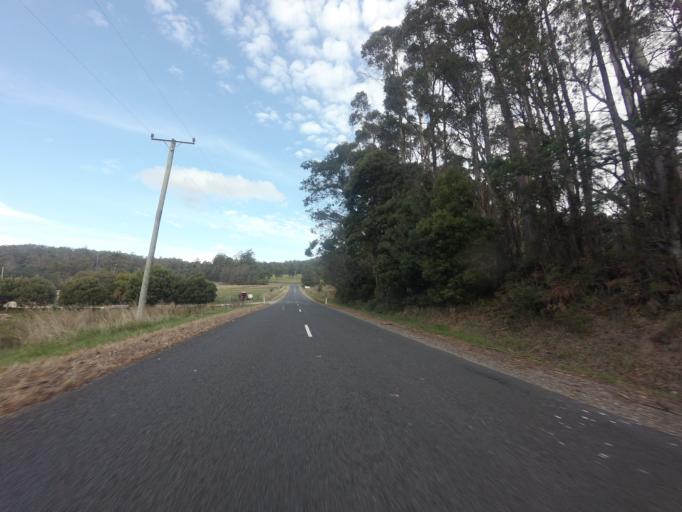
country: AU
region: Tasmania
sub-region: Meander Valley
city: Deloraine
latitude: -41.6335
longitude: 146.7129
